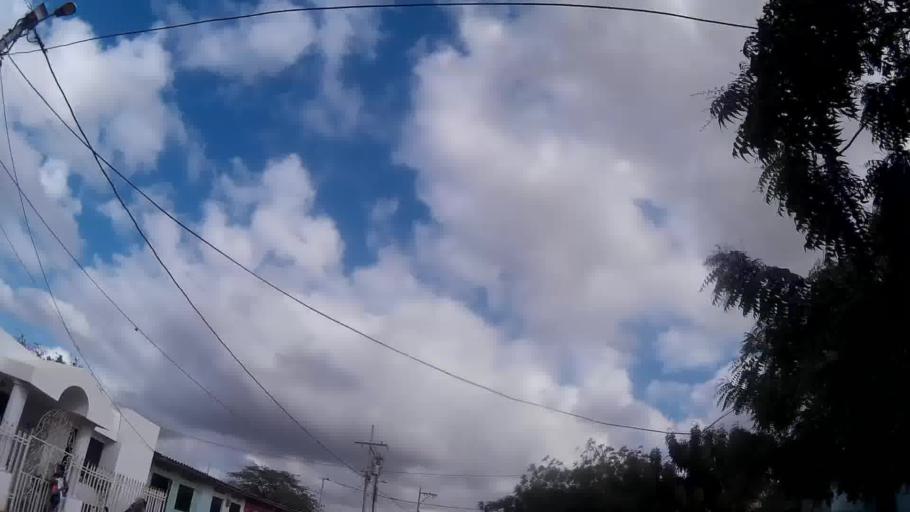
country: CO
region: La Guajira
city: Maicao
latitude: 11.3849
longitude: -72.2383
